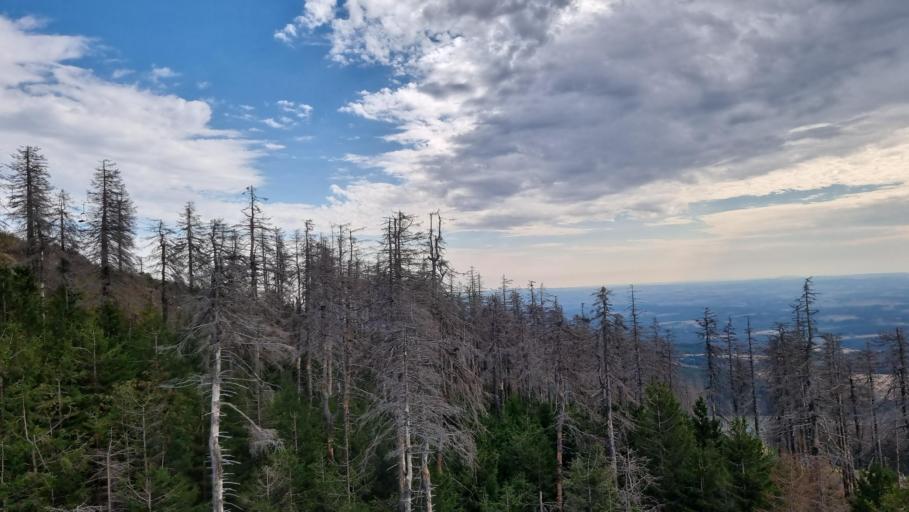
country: DE
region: Lower Saxony
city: Braunlage
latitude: 51.7554
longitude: 10.6172
